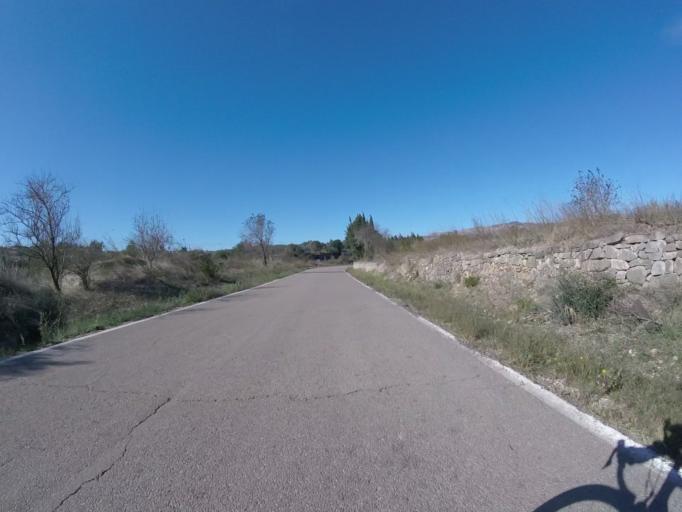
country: ES
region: Valencia
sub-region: Provincia de Castello
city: Chert/Xert
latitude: 40.4647
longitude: 0.1704
